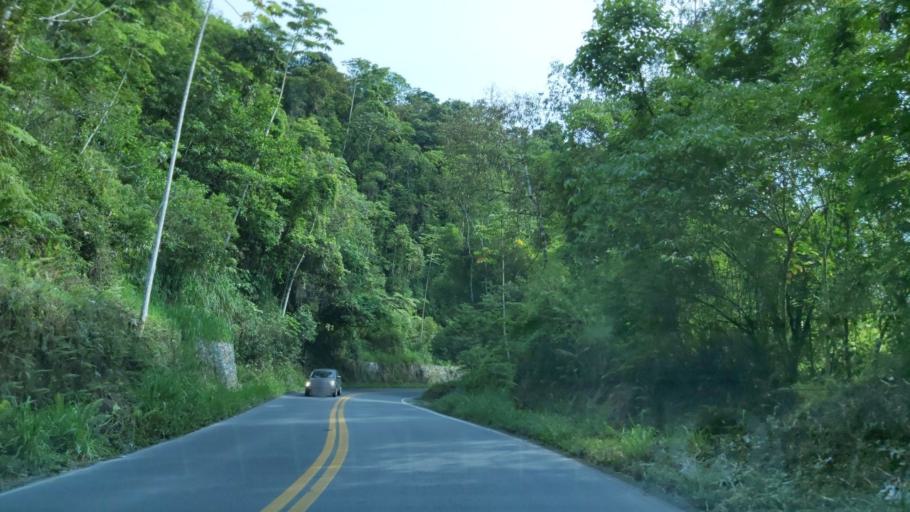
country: BR
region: Sao Paulo
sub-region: Juquia
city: Juquia
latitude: -24.1087
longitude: -47.6261
